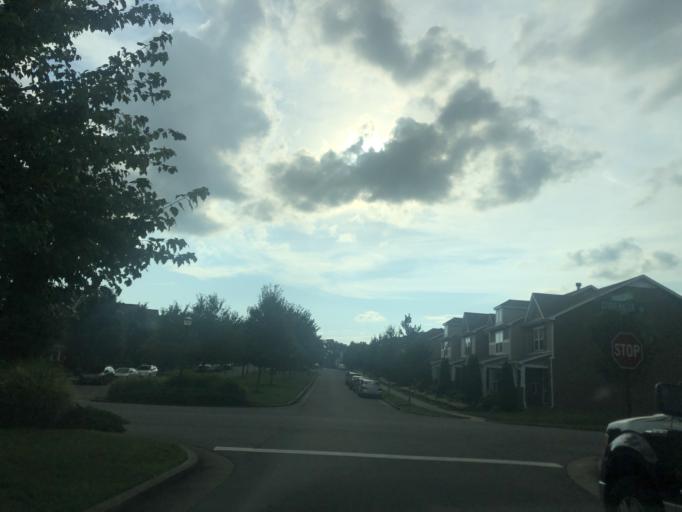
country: US
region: Tennessee
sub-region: Davidson County
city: Lakewood
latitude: 36.1693
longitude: -86.6187
